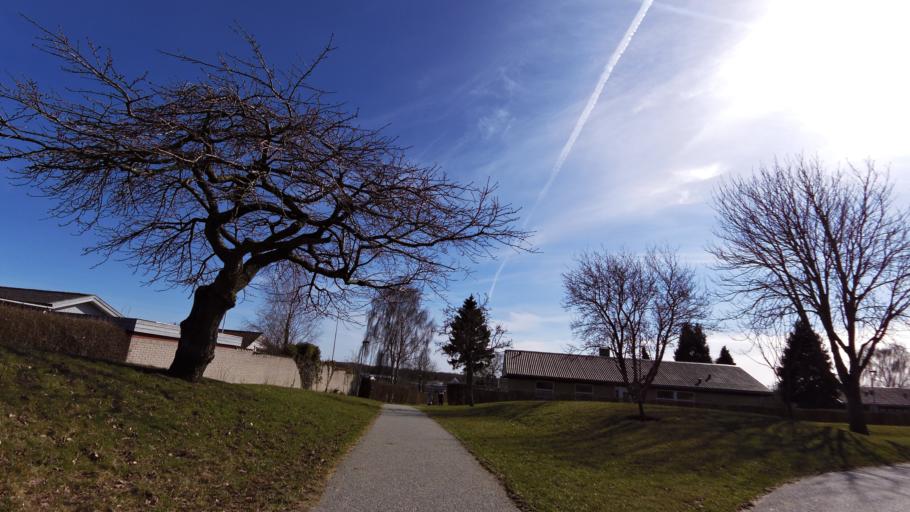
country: DK
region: Central Jutland
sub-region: Arhus Kommune
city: Stavtrup
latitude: 56.1786
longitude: 10.1039
